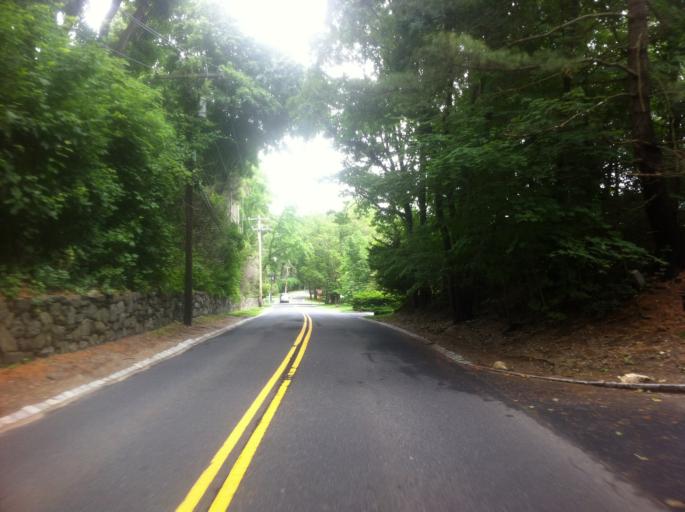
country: US
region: New York
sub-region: Nassau County
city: Bayville
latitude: 40.8876
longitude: -73.5637
